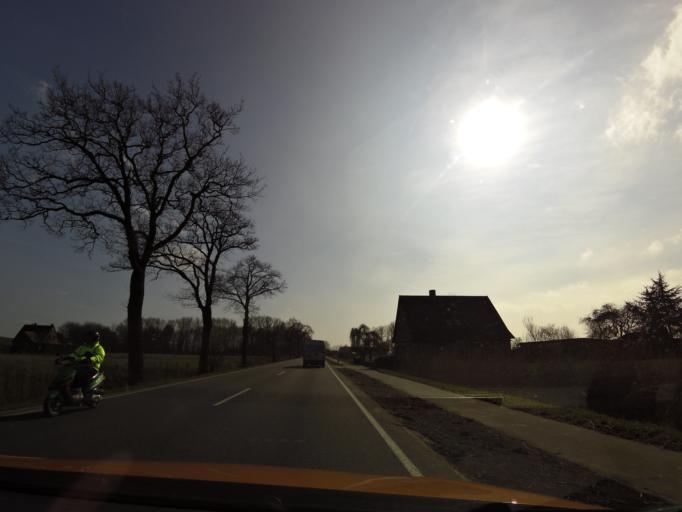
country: DE
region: Lower Saxony
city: Elsfleth
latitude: 53.2125
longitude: 8.4443
